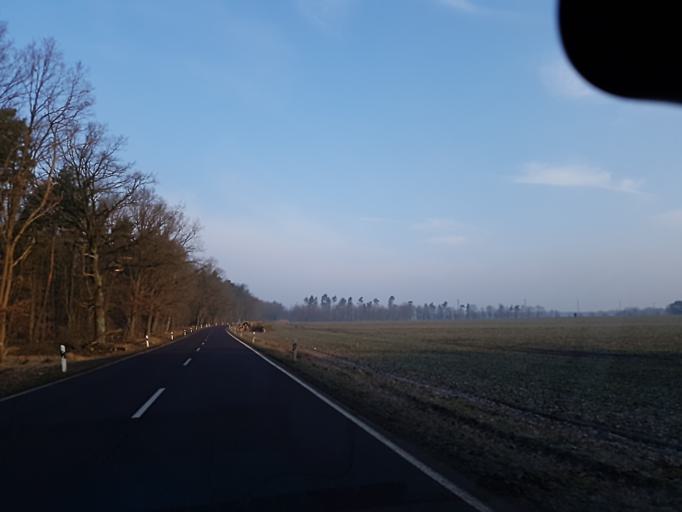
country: DE
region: Brandenburg
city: Wiesenburg
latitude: 52.0644
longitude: 12.4516
